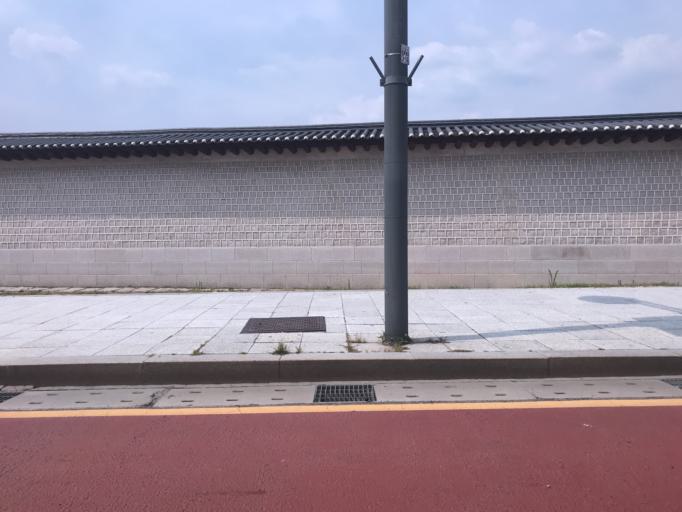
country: KR
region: Seoul
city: Seoul
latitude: 37.5757
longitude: 126.9779
